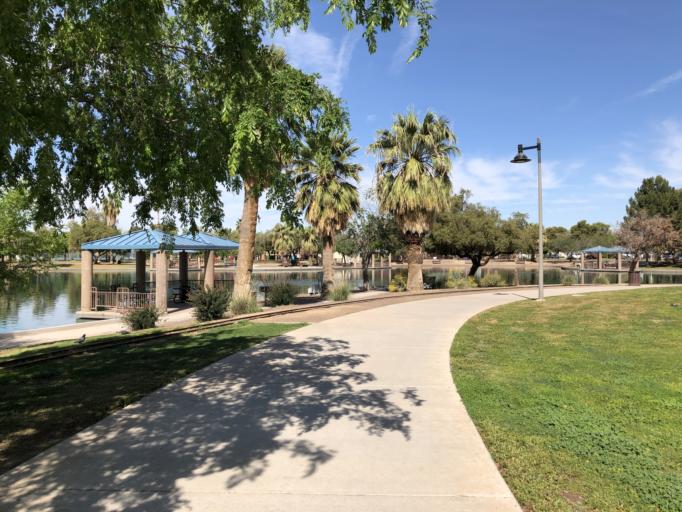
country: US
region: Arizona
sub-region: Maricopa County
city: Guadalupe
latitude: 33.3132
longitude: -111.9188
